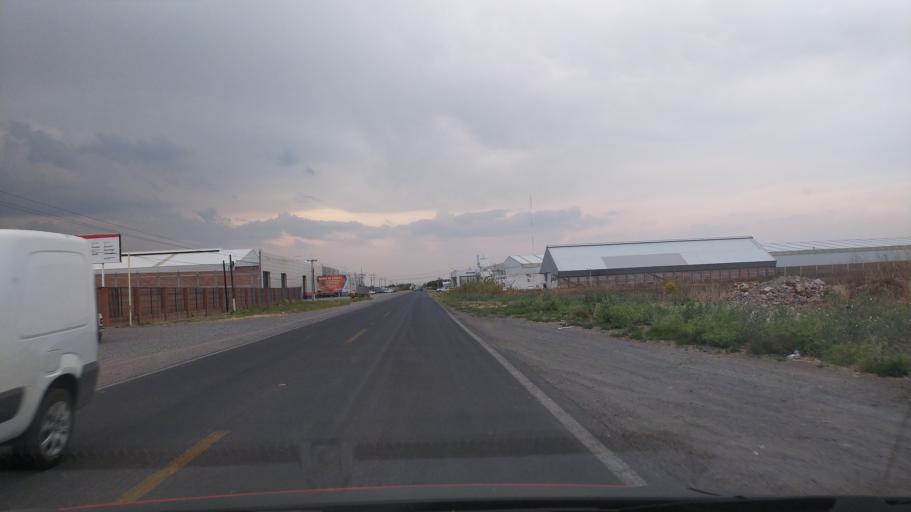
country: MX
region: Guanajuato
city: Ciudad Manuel Doblado
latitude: 20.7443
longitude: -101.9290
